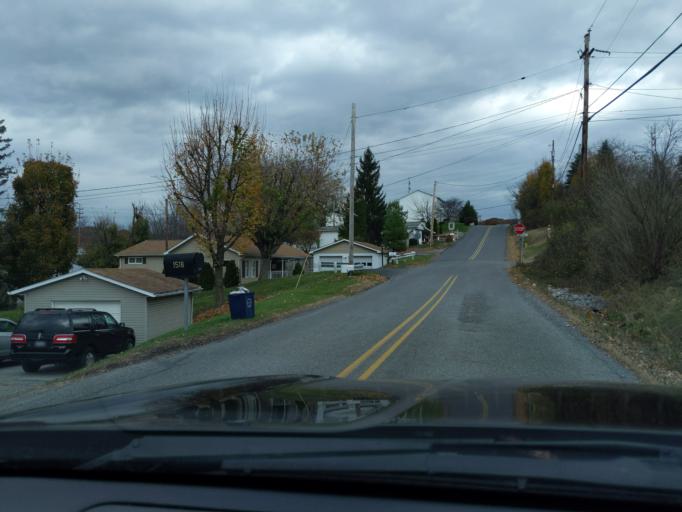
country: US
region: Pennsylvania
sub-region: Blair County
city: Greenwood
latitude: 40.5329
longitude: -78.3673
